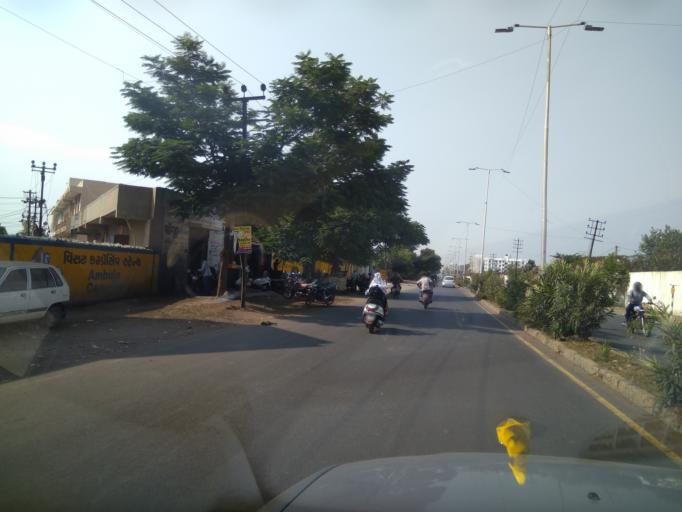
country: IN
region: Gujarat
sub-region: Jamnagar
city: Jamnagar
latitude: 22.4568
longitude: 70.0458
